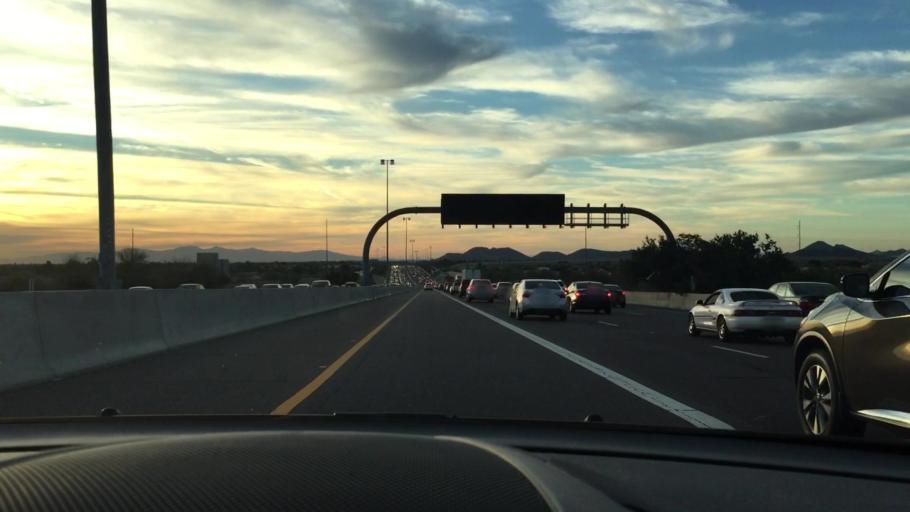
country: US
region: Arizona
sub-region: Maricopa County
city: Paradise Valley
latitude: 33.6678
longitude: -112.0513
